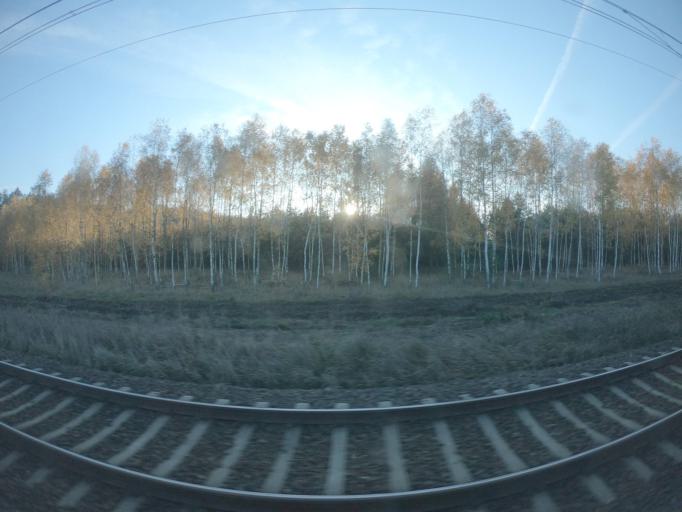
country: PL
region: Lubusz
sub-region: Powiat slubicki
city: Rzepin
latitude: 52.2854
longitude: 14.8970
